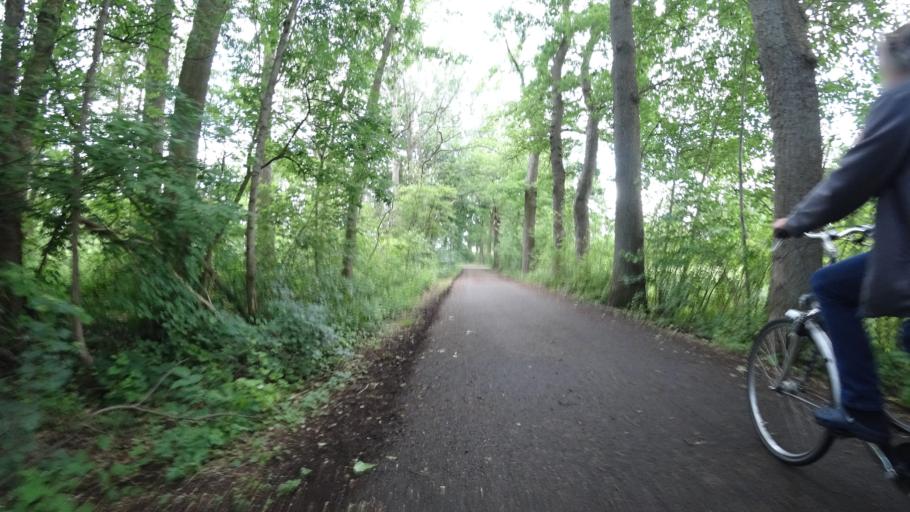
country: DE
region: North Rhine-Westphalia
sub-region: Regierungsbezirk Detmold
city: Guetersloh
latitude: 51.9318
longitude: 8.3509
